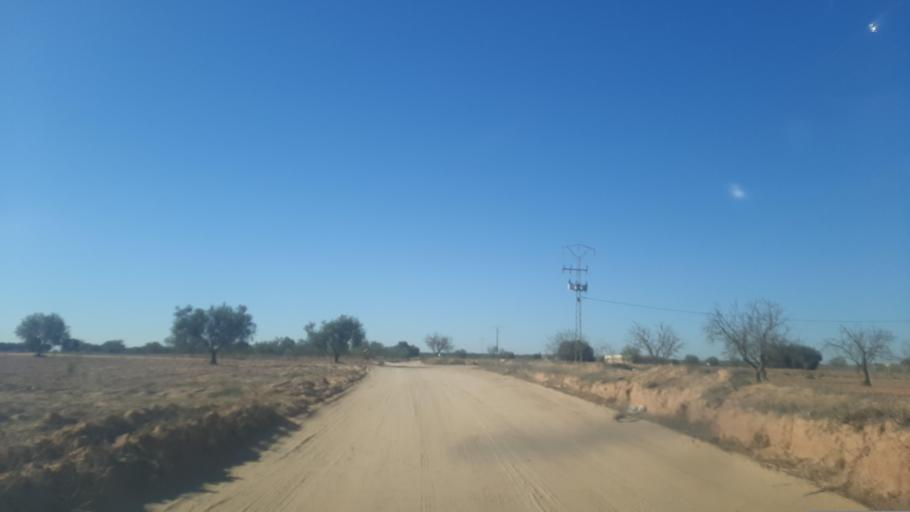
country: TN
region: Safaqis
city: Sfax
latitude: 34.8872
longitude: 10.5867
